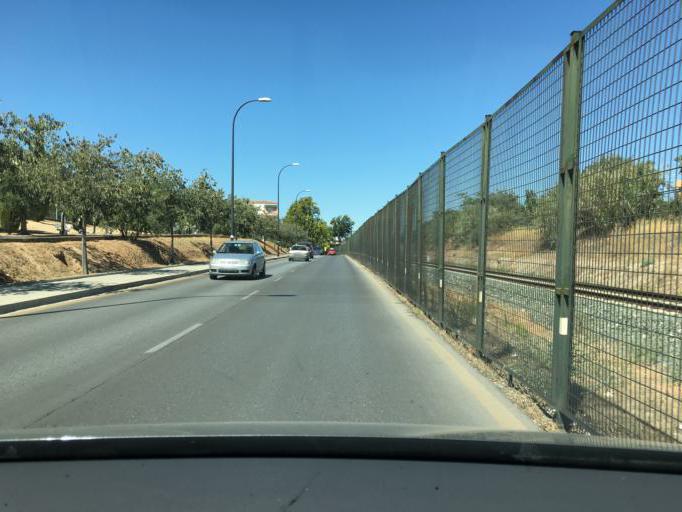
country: ES
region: Andalusia
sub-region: Provincia de Granada
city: Maracena
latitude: 37.1989
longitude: -3.6232
